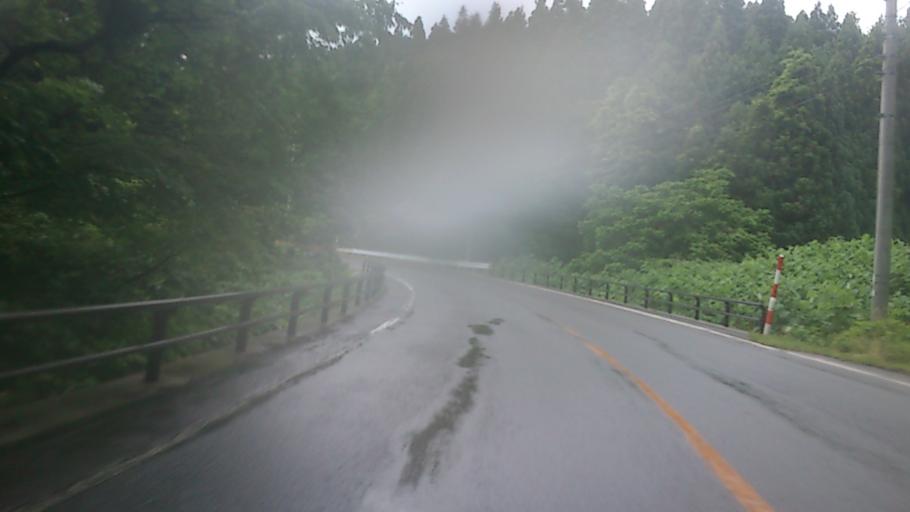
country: JP
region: Akita
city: Noshiromachi
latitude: 40.4129
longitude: 139.9560
